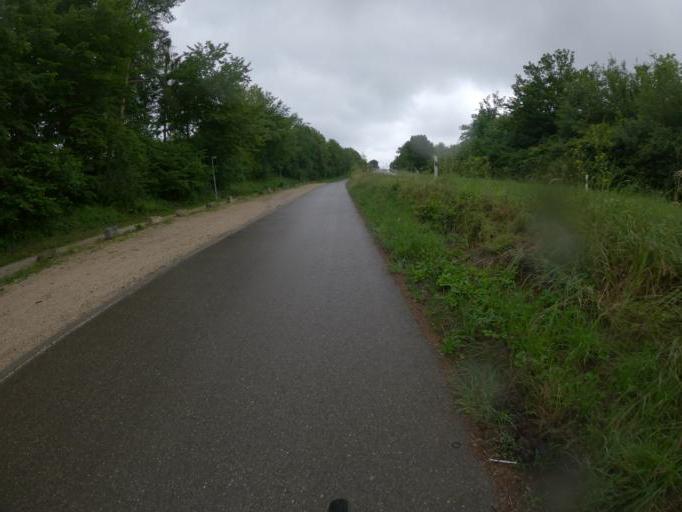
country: DE
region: Baden-Wuerttemberg
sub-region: Regierungsbezirk Stuttgart
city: Adelberg
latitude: 48.7608
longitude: 9.5947
